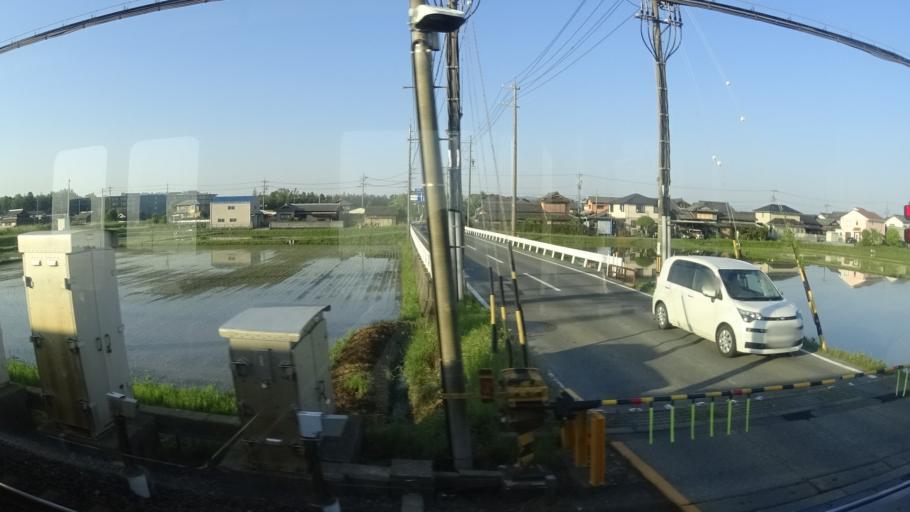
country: JP
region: Mie
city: Ise
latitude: 34.5363
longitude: 136.6292
